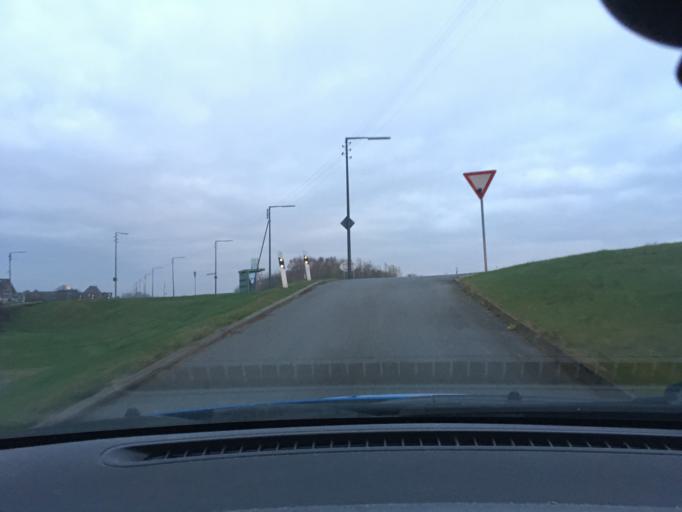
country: DE
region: Lower Saxony
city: Winsen
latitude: 53.3989
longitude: 10.2157
